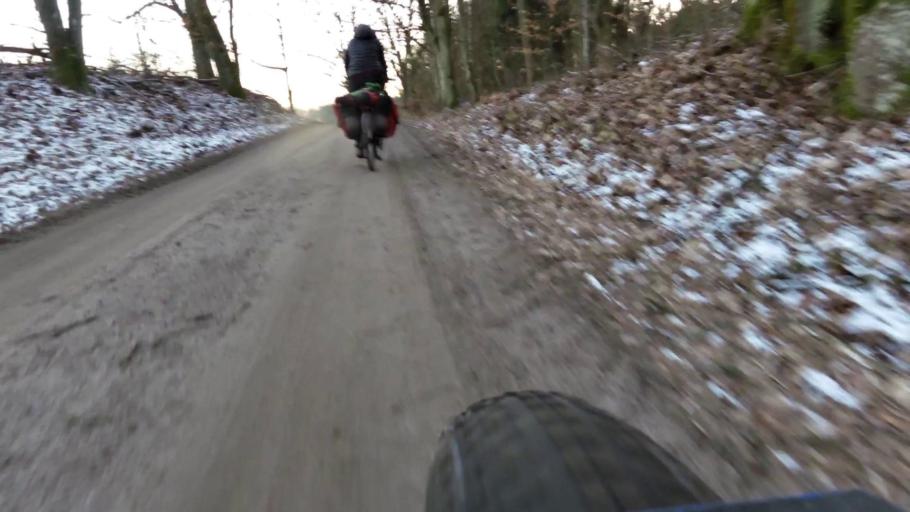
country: PL
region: West Pomeranian Voivodeship
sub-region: Powiat walecki
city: Walcz
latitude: 53.2478
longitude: 16.3728
